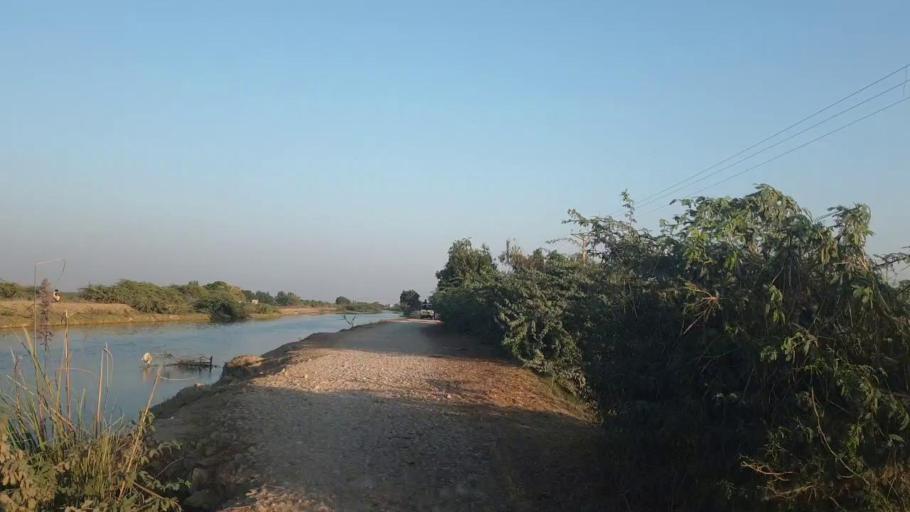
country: PK
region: Sindh
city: Mirpur Sakro
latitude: 24.4619
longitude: 67.5905
